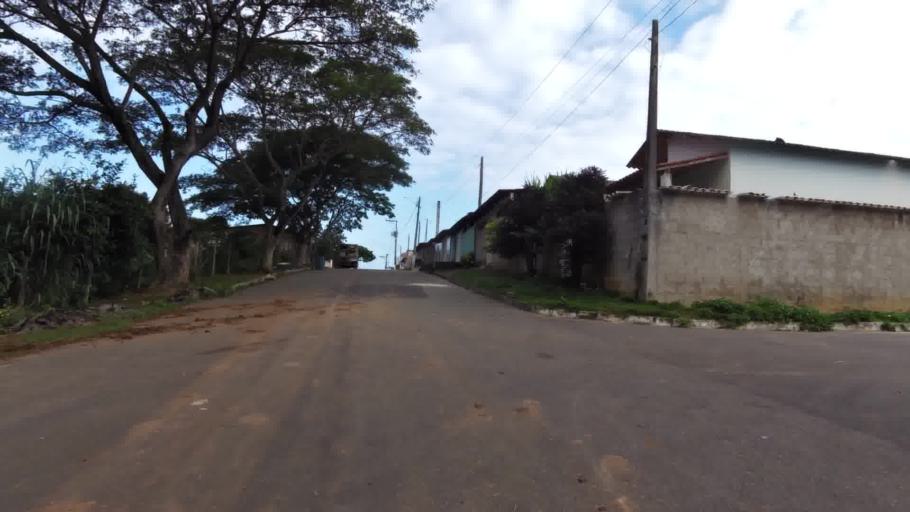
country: BR
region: Espirito Santo
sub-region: Piuma
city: Piuma
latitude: -20.7925
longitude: -40.6378
